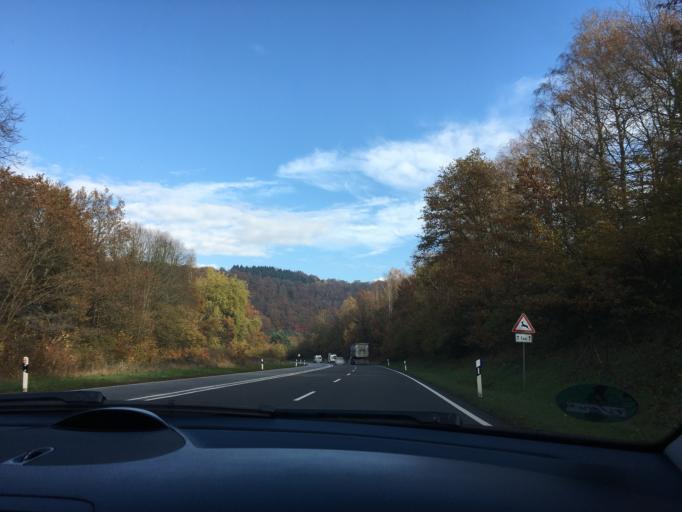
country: DE
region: Rheinland-Pfalz
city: Steinalben
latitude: 49.3090
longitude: 7.6672
